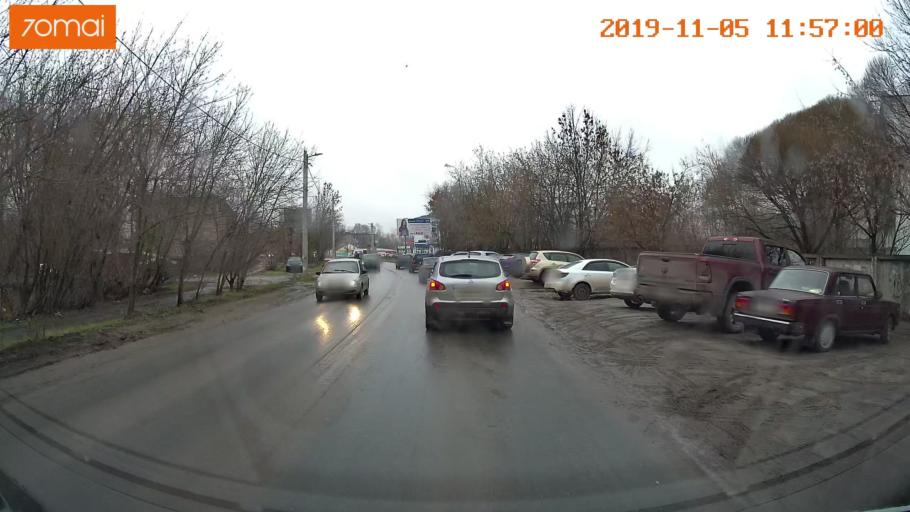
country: RU
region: Ivanovo
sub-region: Gorod Ivanovo
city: Ivanovo
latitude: 56.9844
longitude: 41.0332
